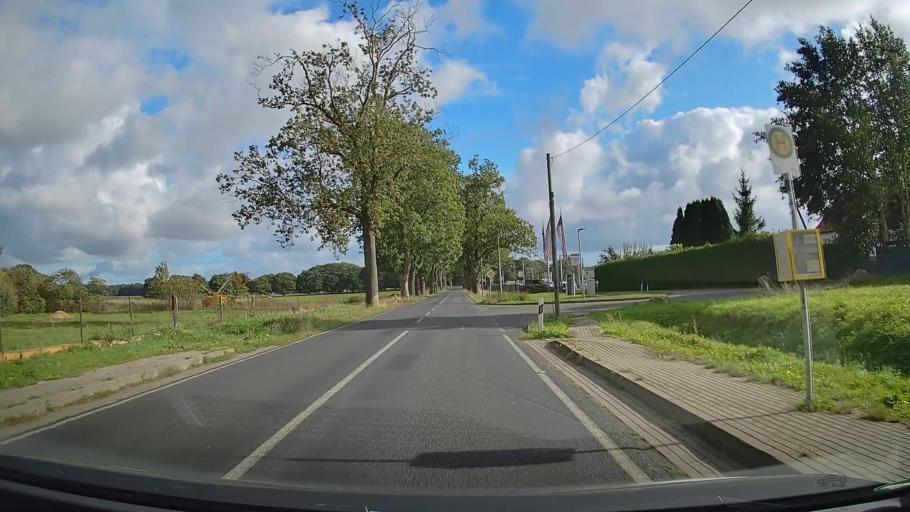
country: DE
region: Mecklenburg-Vorpommern
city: Putbus
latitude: 54.3923
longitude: 13.4645
